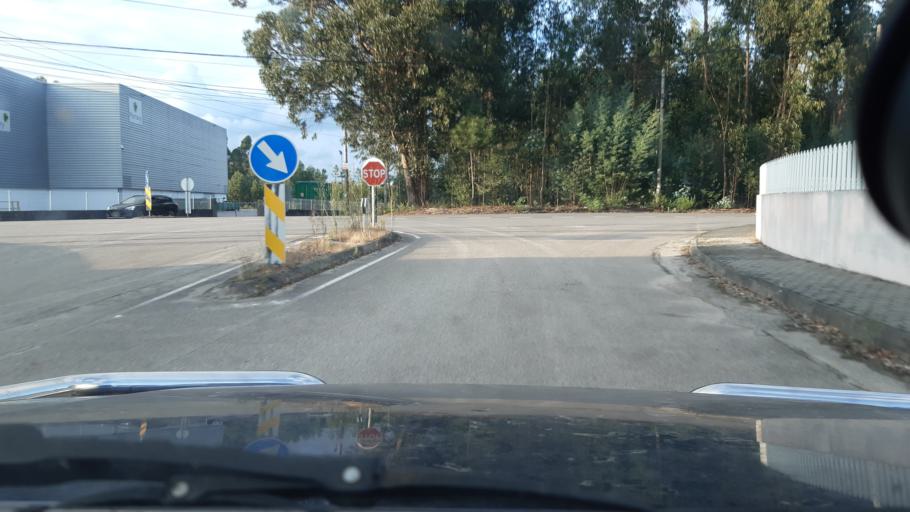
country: PT
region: Aveiro
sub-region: Agueda
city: Agueda
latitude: 40.5816
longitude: -8.4690
